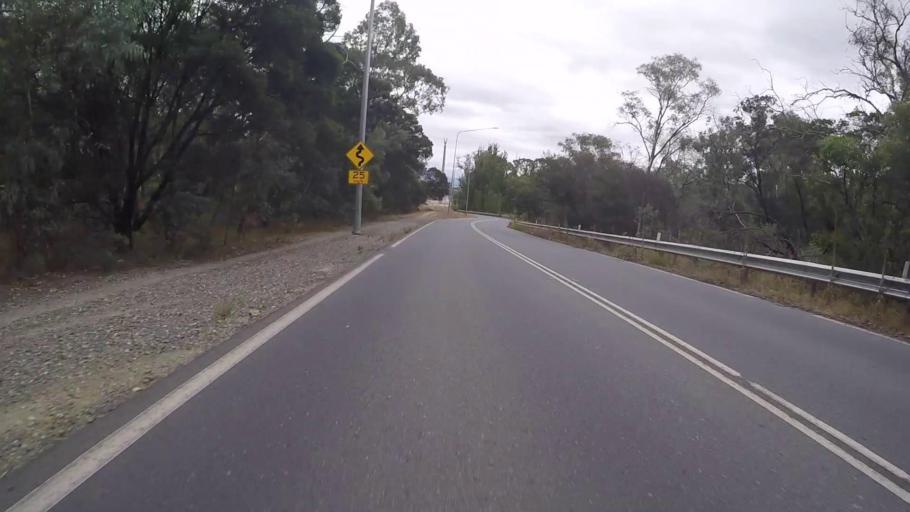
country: AU
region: Australian Capital Territory
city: Canberra
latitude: -35.2957
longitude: 149.1564
